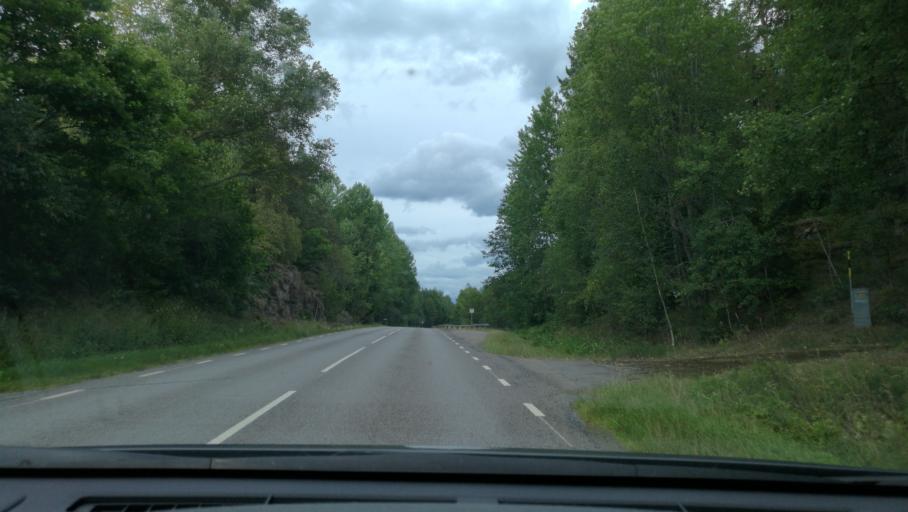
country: SE
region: OEstergoetland
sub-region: Norrkopings Kommun
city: Svartinge
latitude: 58.7055
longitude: 15.9291
